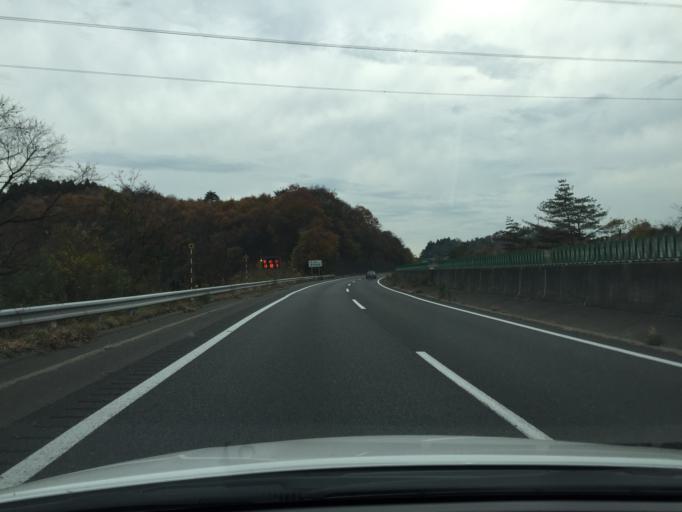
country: JP
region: Fukushima
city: Fukushima-shi
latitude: 37.6683
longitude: 140.4529
